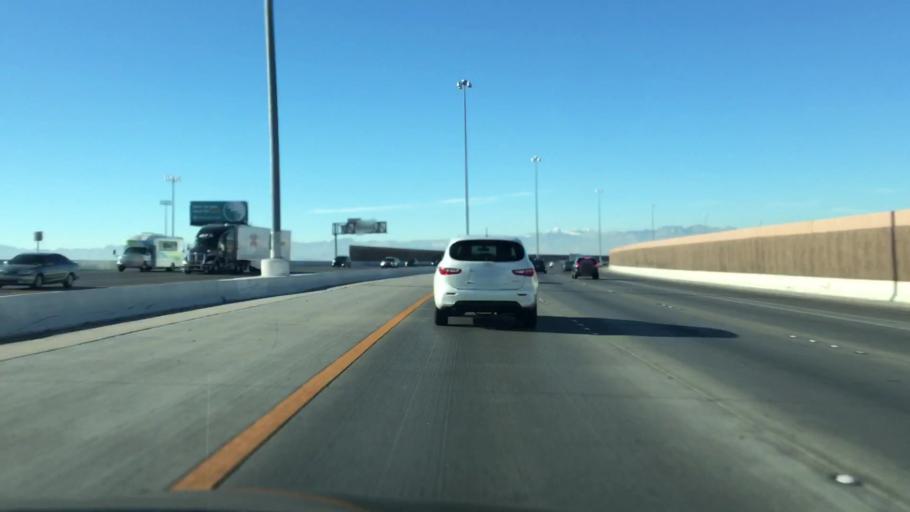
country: US
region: Nevada
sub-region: Clark County
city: Whitney
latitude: 36.0244
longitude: -115.1244
